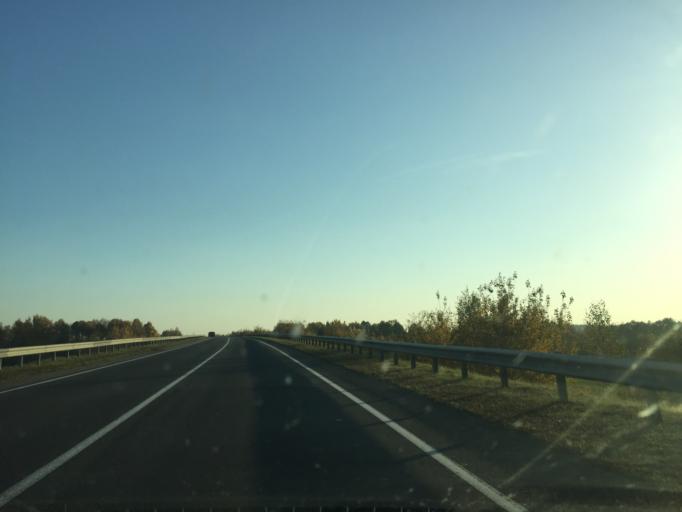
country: BY
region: Mogilev
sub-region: Mahilyowski Rayon
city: Kadino
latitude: 53.8620
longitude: 30.4804
